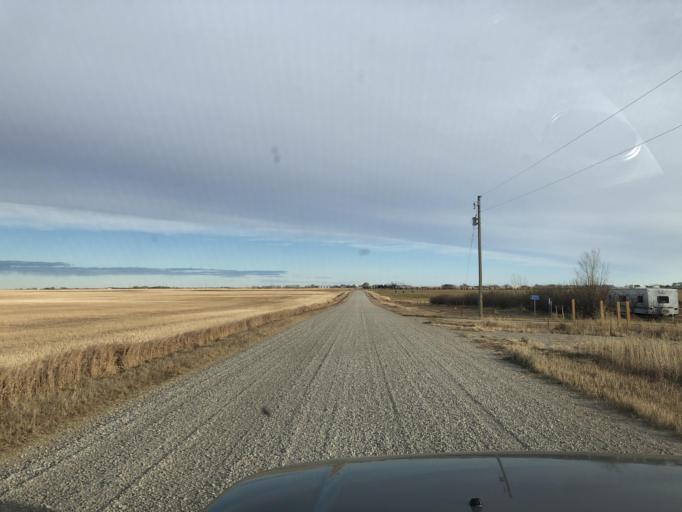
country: CA
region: Alberta
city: Strathmore
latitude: 50.8925
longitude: -113.5488
